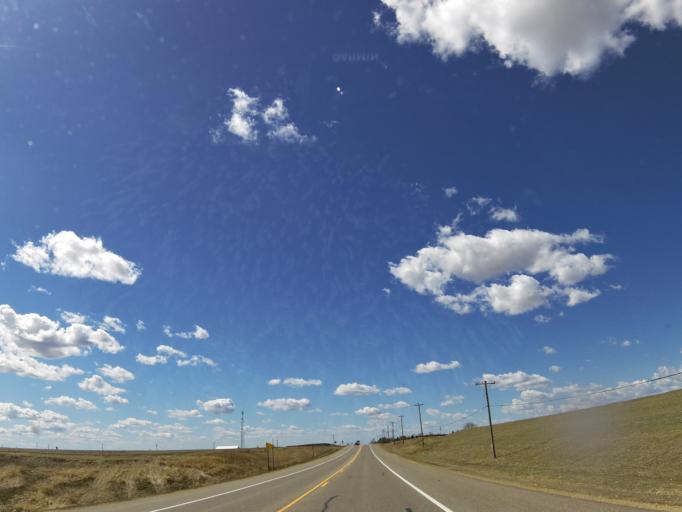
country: US
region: Minnesota
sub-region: Dakota County
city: Rosemount
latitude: 44.7174
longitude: -93.1103
